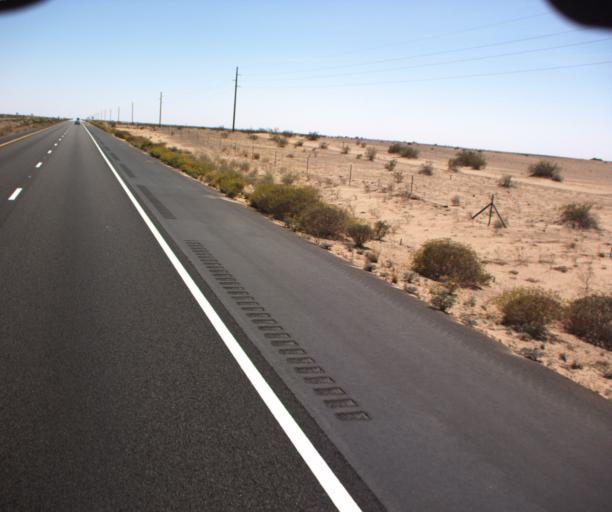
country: US
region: Arizona
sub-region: Yuma County
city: Somerton
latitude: 32.5321
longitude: -114.5622
